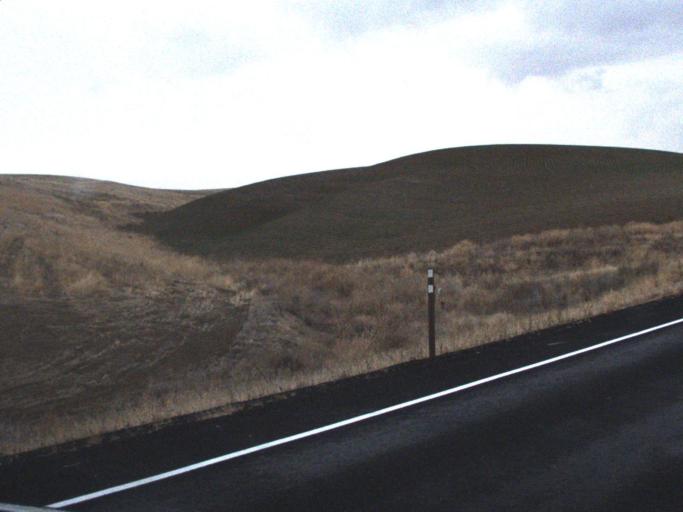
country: US
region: Washington
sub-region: Garfield County
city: Pomeroy
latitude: 46.7917
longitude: -117.8921
